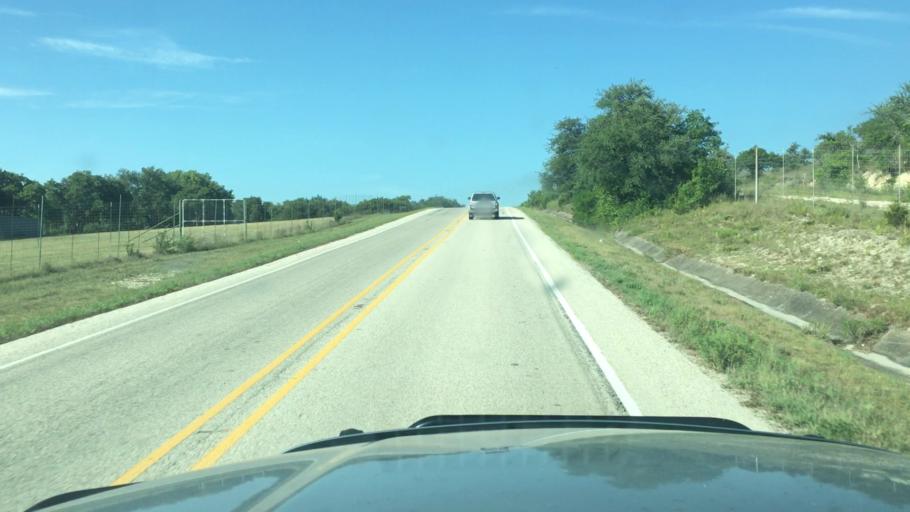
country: US
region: Texas
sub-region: Hays County
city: Dripping Springs
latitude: 30.1527
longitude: -98.2538
